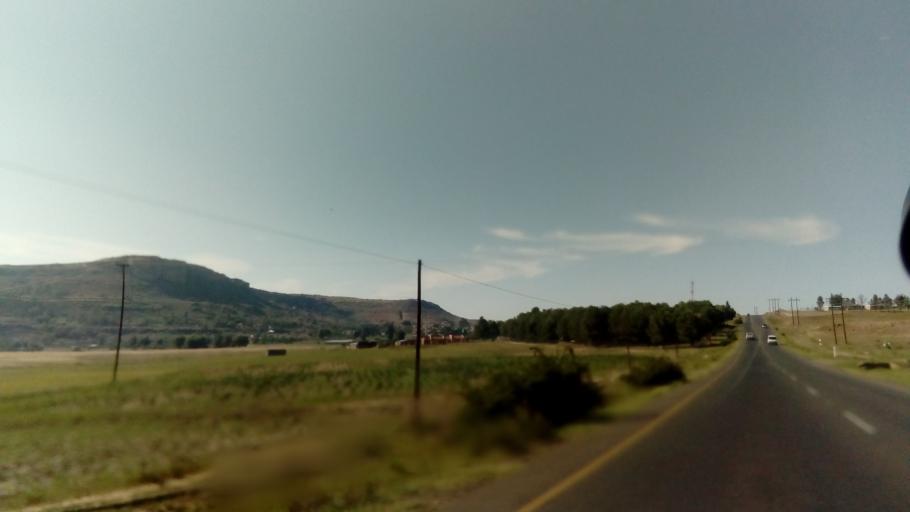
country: LS
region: Maseru
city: Maseru
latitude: -29.2361
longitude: 27.6080
